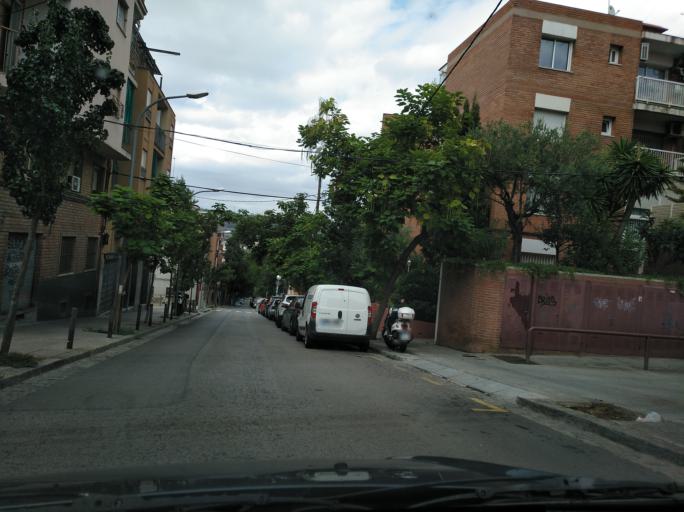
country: ES
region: Catalonia
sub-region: Provincia de Barcelona
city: Horta-Guinardo
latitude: 41.4218
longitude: 2.1584
